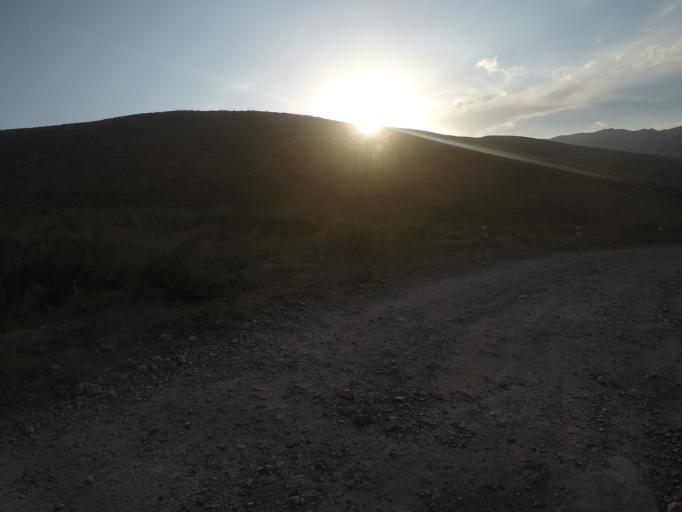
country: KG
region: Chuy
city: Bishkek
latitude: 42.6563
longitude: 74.6521
